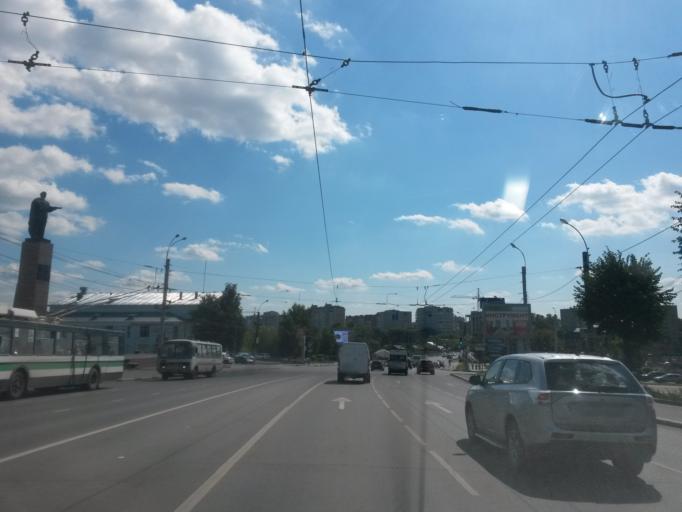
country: RU
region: Ivanovo
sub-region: Gorod Ivanovo
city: Ivanovo
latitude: 57.0070
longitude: 40.9907
